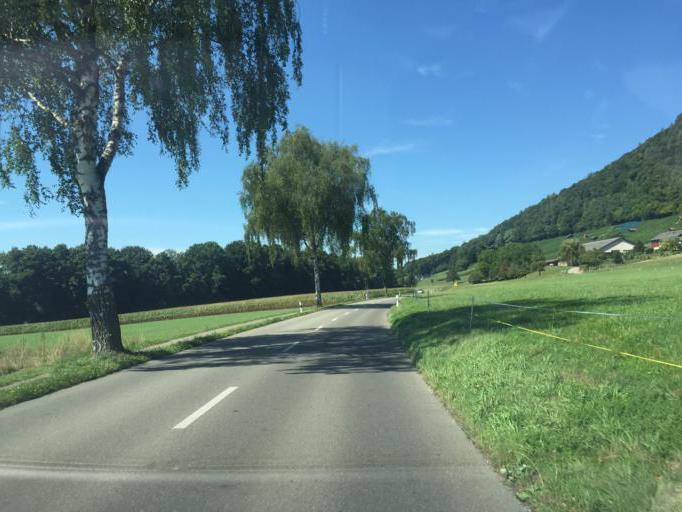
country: CH
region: Thurgau
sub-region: Frauenfeld District
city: Wagenhausen
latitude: 47.6678
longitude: 8.8449
